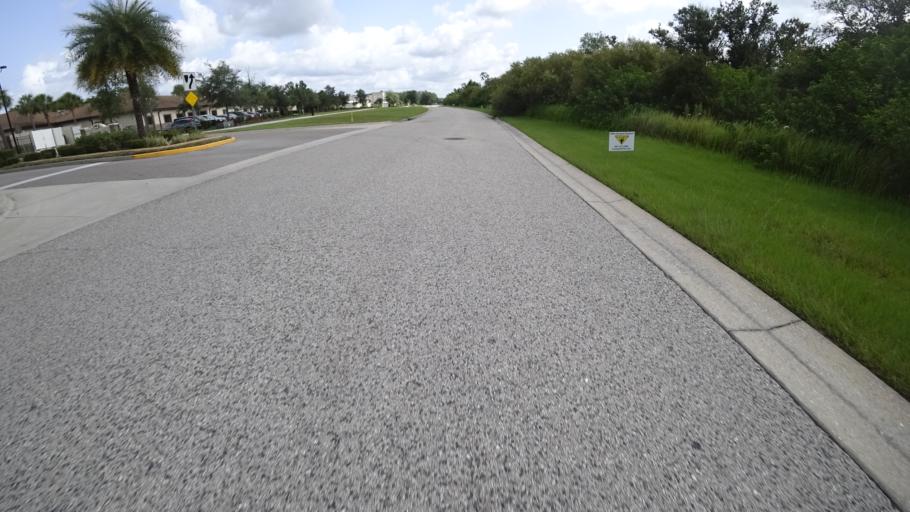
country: US
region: Florida
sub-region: Sarasota County
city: Desoto Lakes
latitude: 27.4440
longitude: -82.4560
